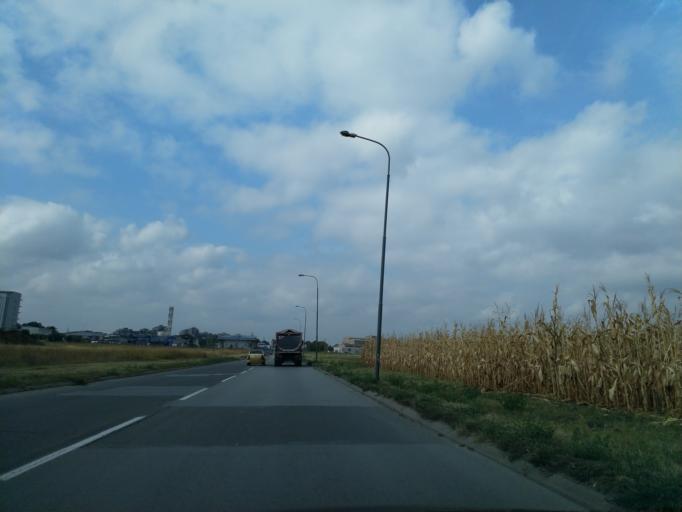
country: RS
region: Central Serbia
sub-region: Sumadijski Okrug
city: Kragujevac
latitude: 44.0259
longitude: 20.9250
